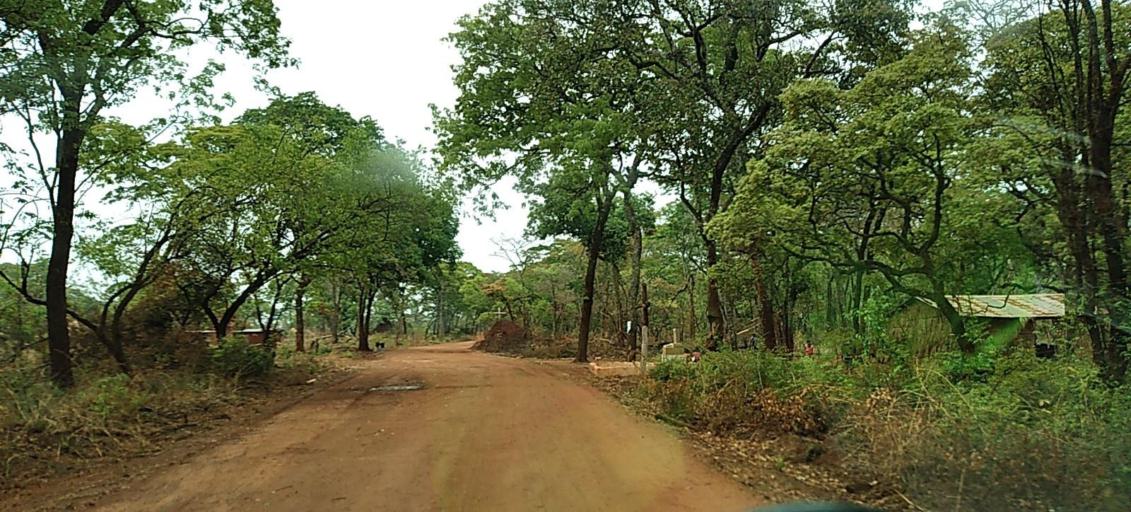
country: ZM
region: North-Western
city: Solwezi
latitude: -12.3112
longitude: 26.5222
